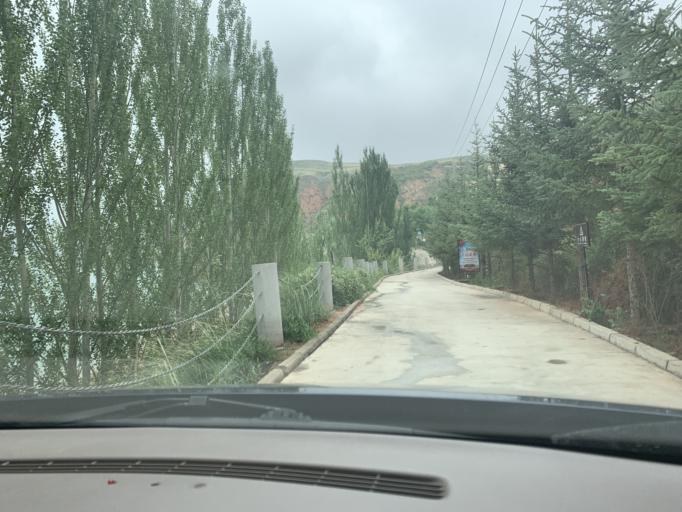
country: CN
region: Gansu Sheng
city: Gulang
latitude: 37.5621
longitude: 102.7426
